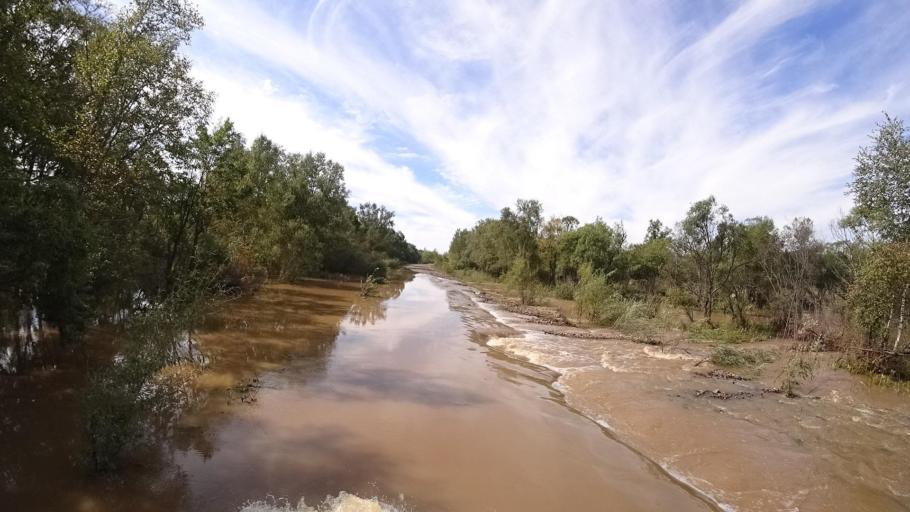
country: RU
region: Primorskiy
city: Kirovskiy
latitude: 44.7659
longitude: 133.6173
